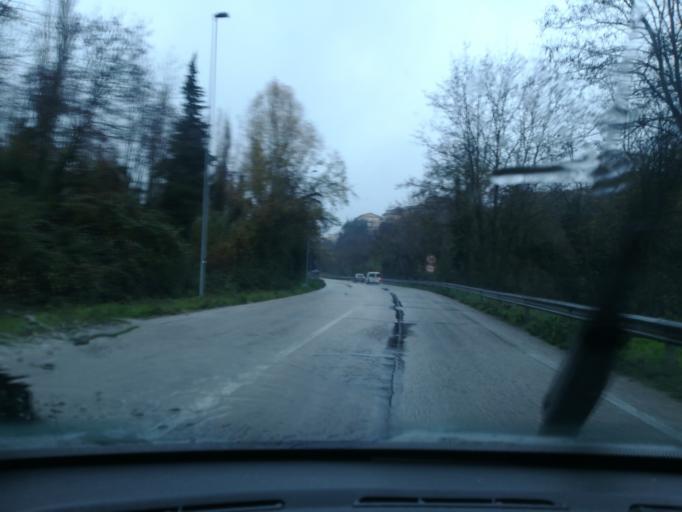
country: IT
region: The Marches
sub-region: Provincia di Macerata
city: Macerata
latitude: 43.2928
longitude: 13.4435
